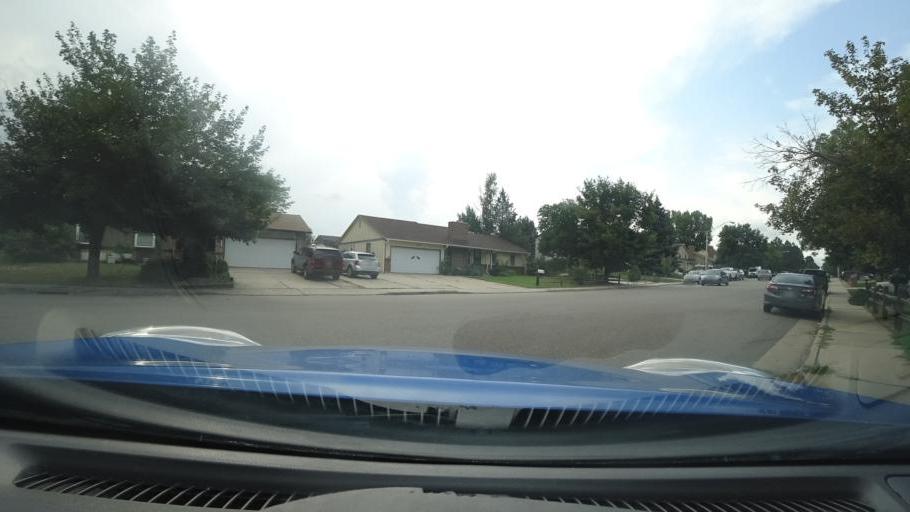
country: US
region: Colorado
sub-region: Adams County
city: Aurora
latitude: 39.6905
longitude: -104.8149
